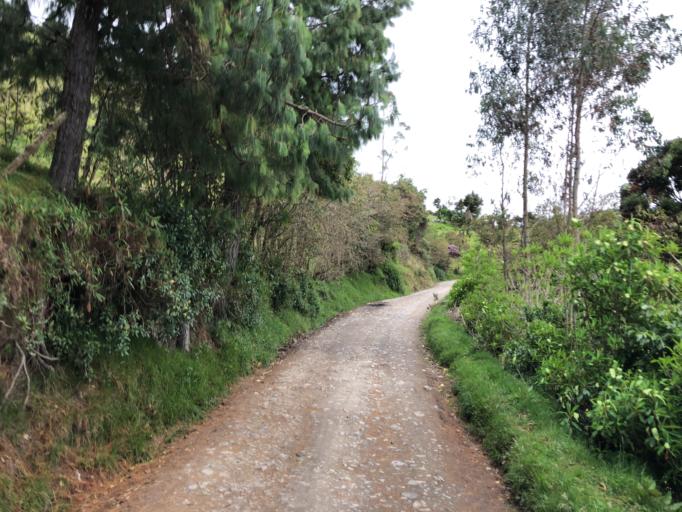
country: CO
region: Cauca
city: Totoro
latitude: 2.5044
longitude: -76.3594
